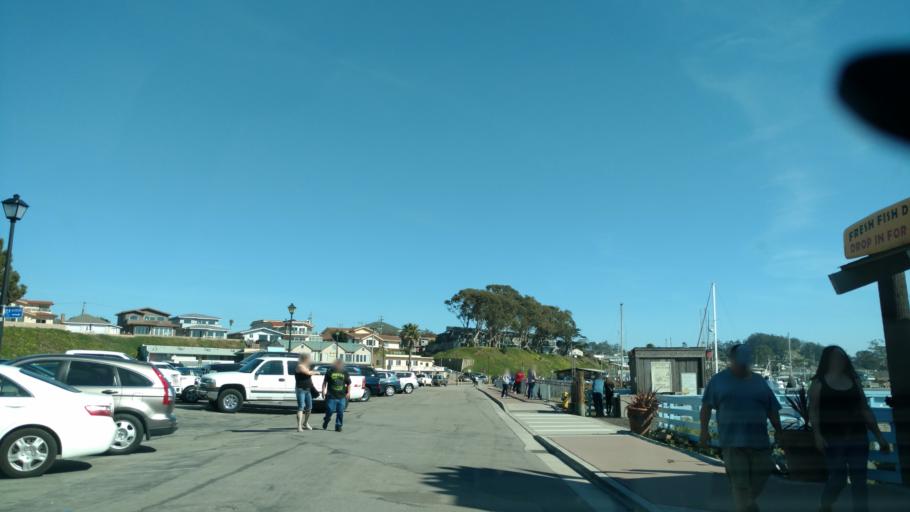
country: US
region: California
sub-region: San Luis Obispo County
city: Morro Bay
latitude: 35.3699
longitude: -120.8559
